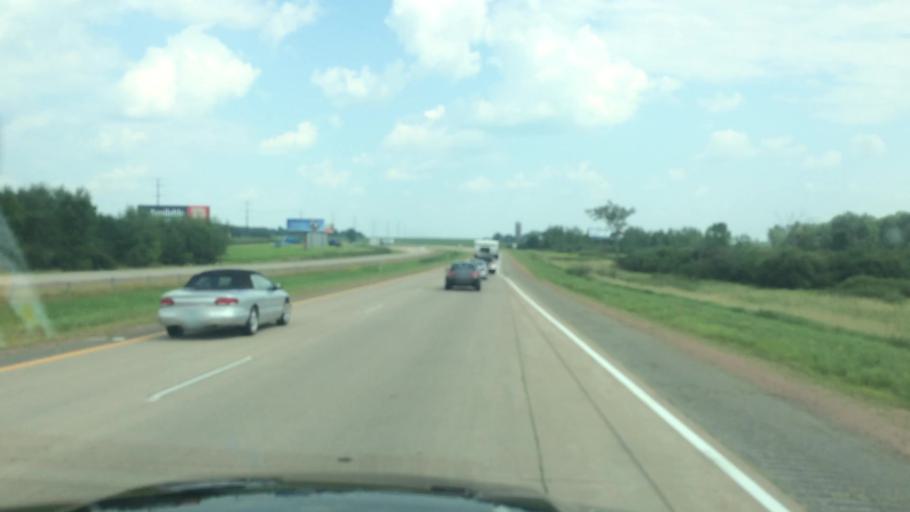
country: US
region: Wisconsin
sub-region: Clark County
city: Abbotsford
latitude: 44.9326
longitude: -90.3053
